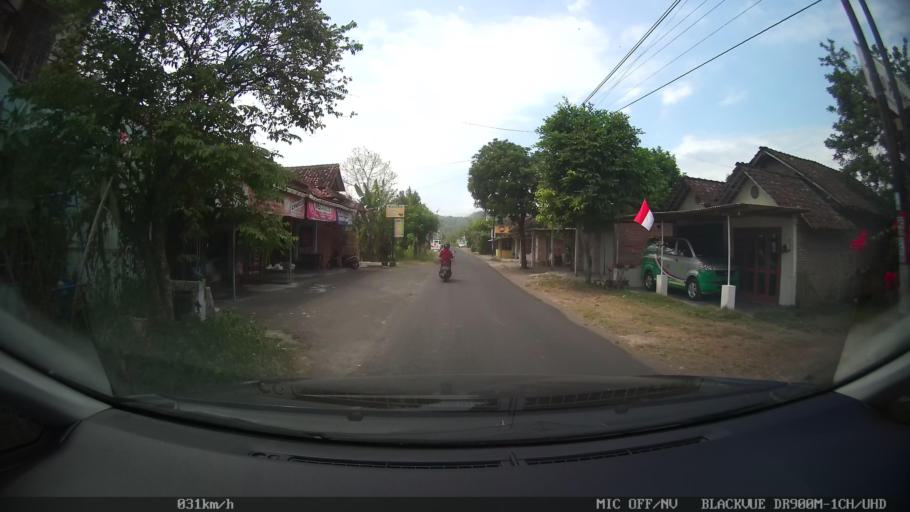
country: ID
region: Central Java
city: Candi Prambanan
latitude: -7.8122
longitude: 110.4896
